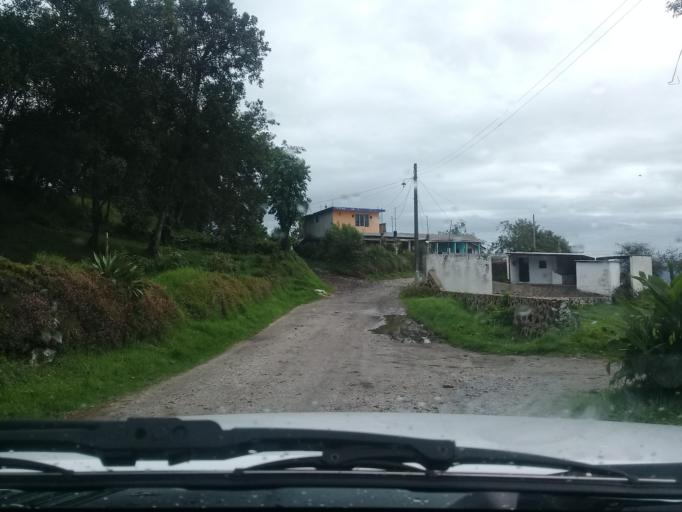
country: MX
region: Veracruz
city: Rafael Lucio
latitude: 19.6207
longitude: -96.9985
